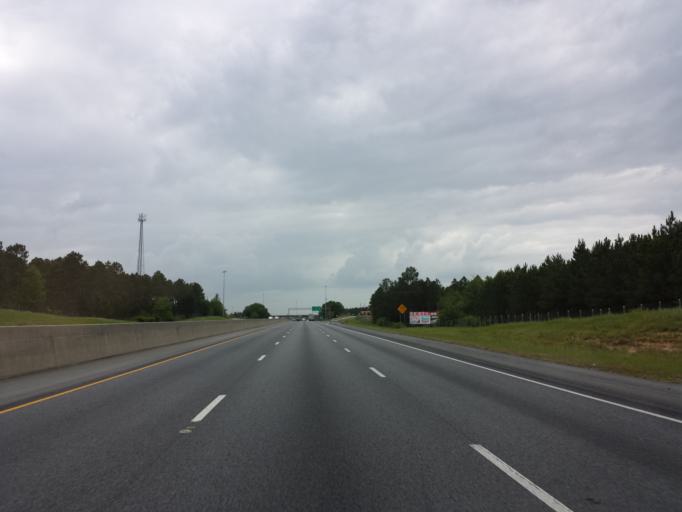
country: US
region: Georgia
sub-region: Tift County
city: Tifton
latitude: 31.5451
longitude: -83.5315
